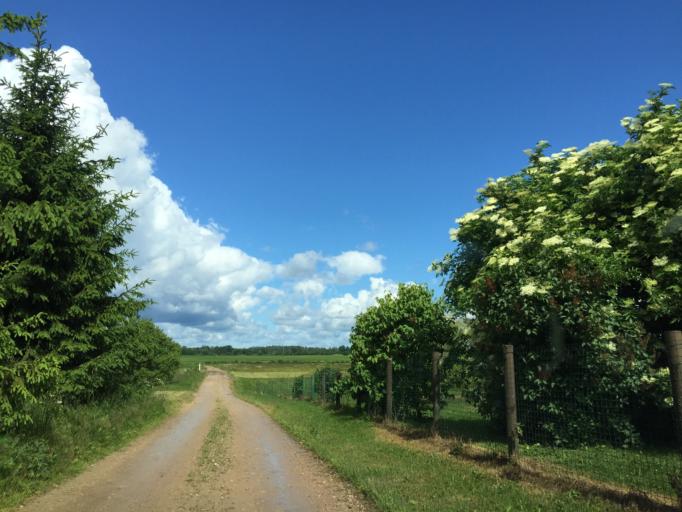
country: LV
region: Lecava
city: Iecava
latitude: 56.6144
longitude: 24.2104
